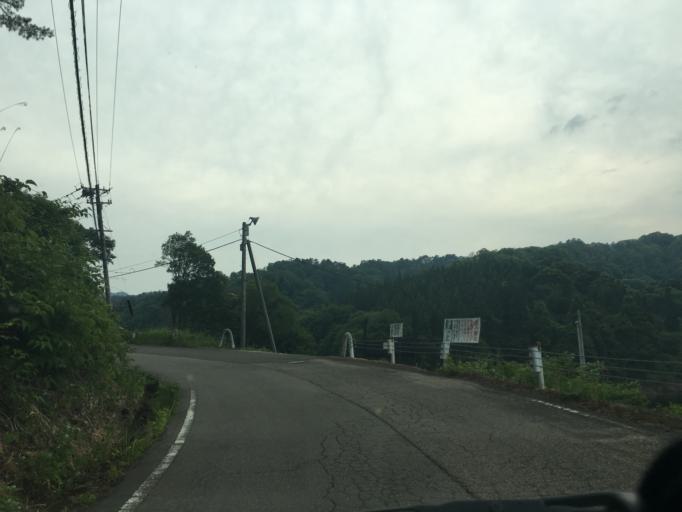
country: JP
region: Fukushima
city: Kitakata
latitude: 37.4880
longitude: 139.7792
